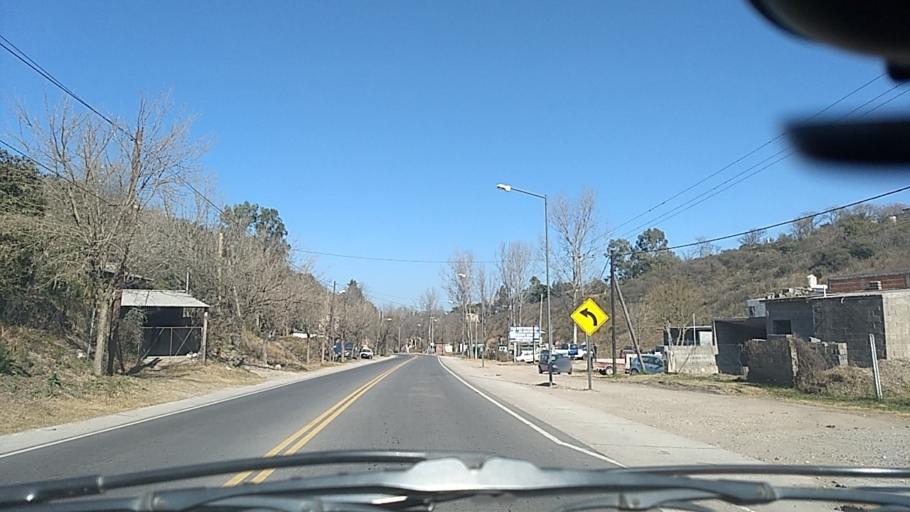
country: AR
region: Cordoba
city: Agua de Oro
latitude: -31.1004
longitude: -64.2913
